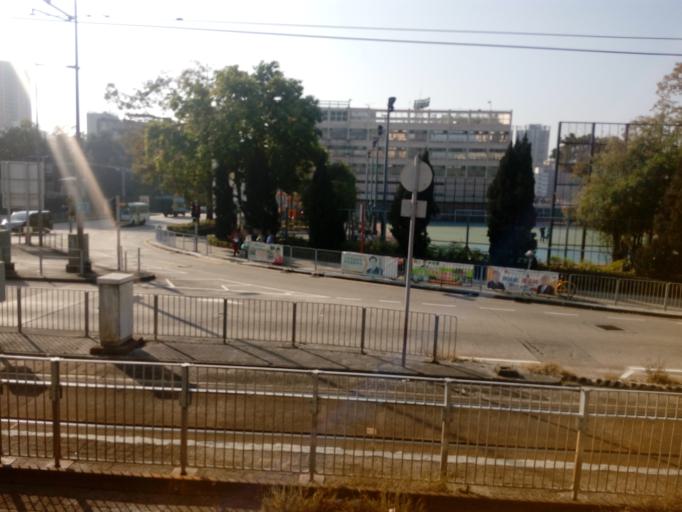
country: HK
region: Yuen Long
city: Yuen Long Kau Hui
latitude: 22.4446
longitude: 114.0220
